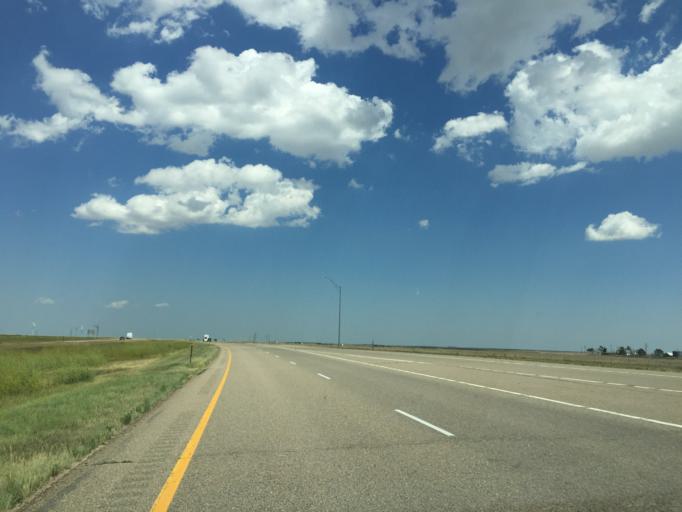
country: US
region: Colorado
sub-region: Lincoln County
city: Hugo
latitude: 39.2751
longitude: -103.4871
